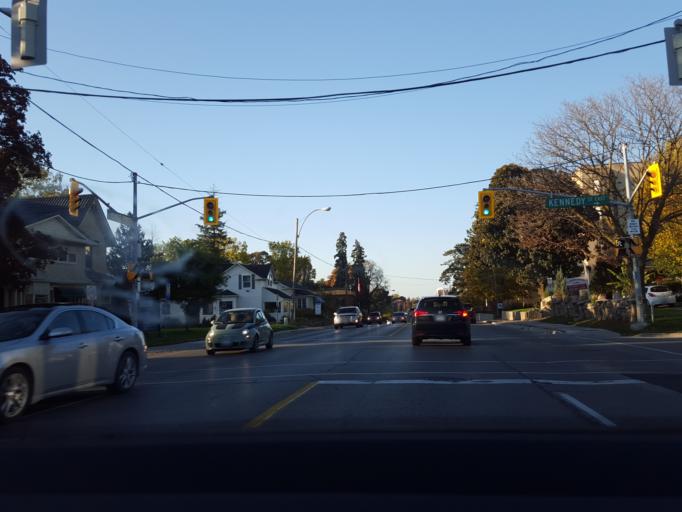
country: CA
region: Ontario
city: Newmarket
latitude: 43.9938
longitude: -79.4661
